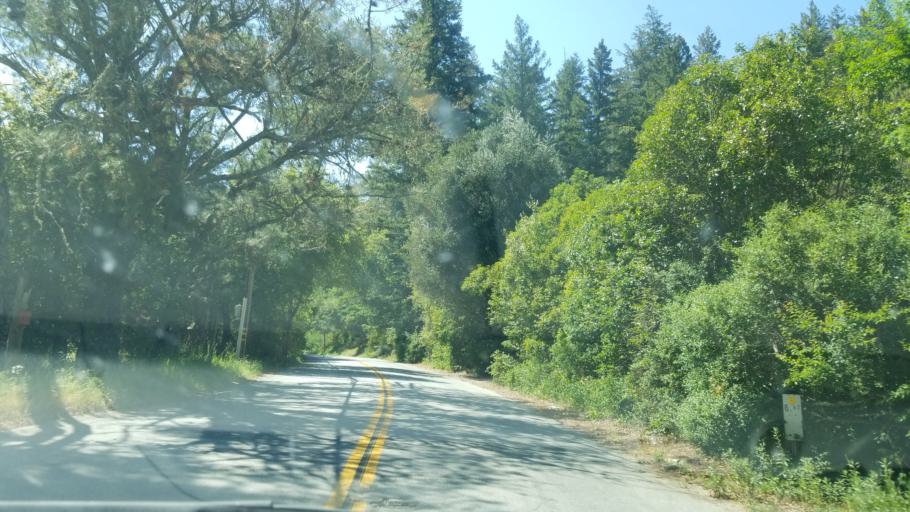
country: US
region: California
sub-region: Santa Clara County
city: Lexington Hills
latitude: 37.1095
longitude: -121.9075
